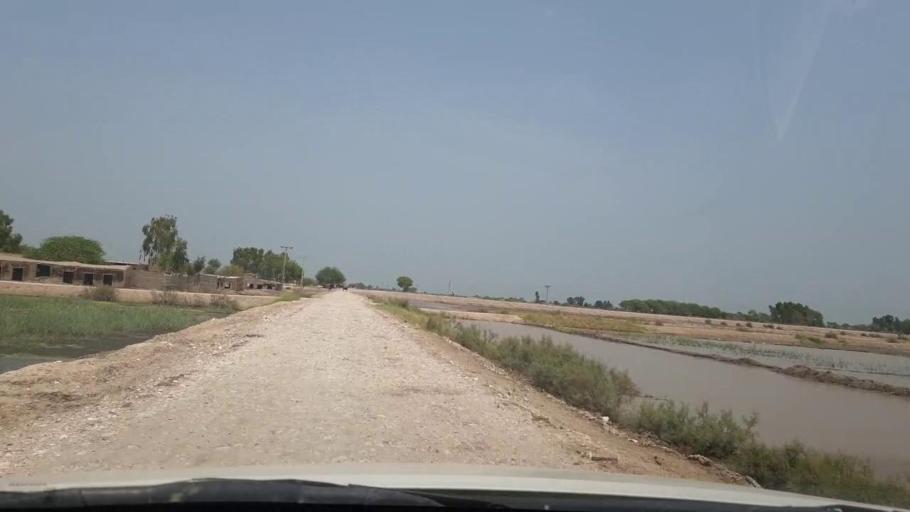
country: PK
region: Sindh
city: Rustam jo Goth
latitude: 28.0771
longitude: 68.8181
